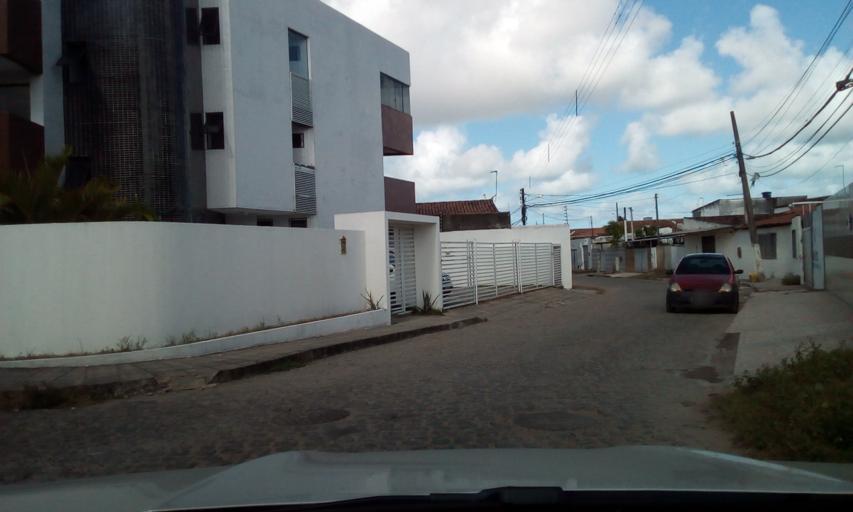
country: BR
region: Paraiba
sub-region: Joao Pessoa
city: Joao Pessoa
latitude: -7.1784
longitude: -34.8555
